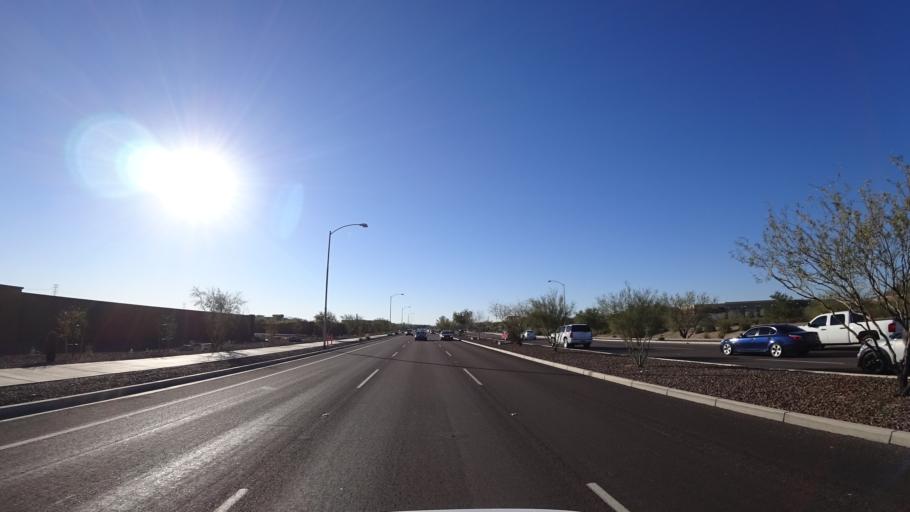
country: US
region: Arizona
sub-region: Maricopa County
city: Sun City West
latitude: 33.7106
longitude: -112.2656
